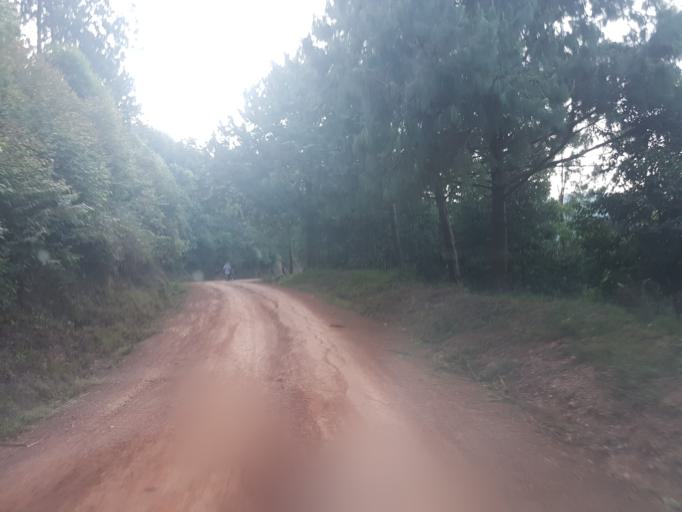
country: UG
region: Western Region
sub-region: Kanungu District
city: Kanungu
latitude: -1.0490
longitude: 29.8849
